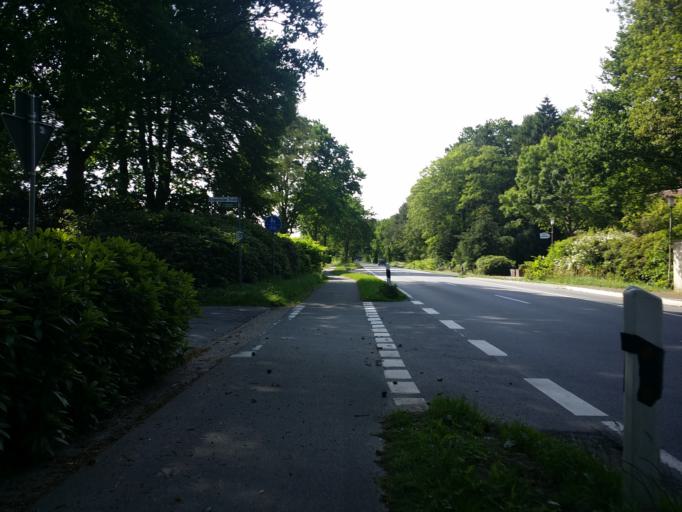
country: DE
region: Lower Saxony
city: Wiefelstede
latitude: 53.2853
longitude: 8.0940
